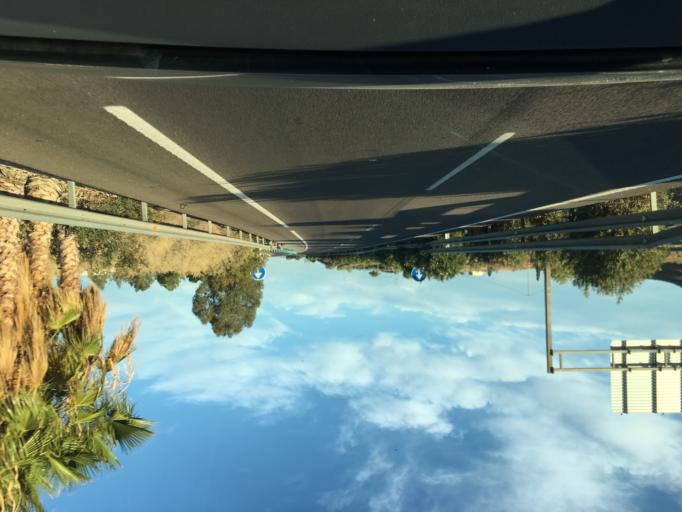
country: ES
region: Andalusia
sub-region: Provincia de Almeria
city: Bedar
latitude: 37.1584
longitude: -1.9504
